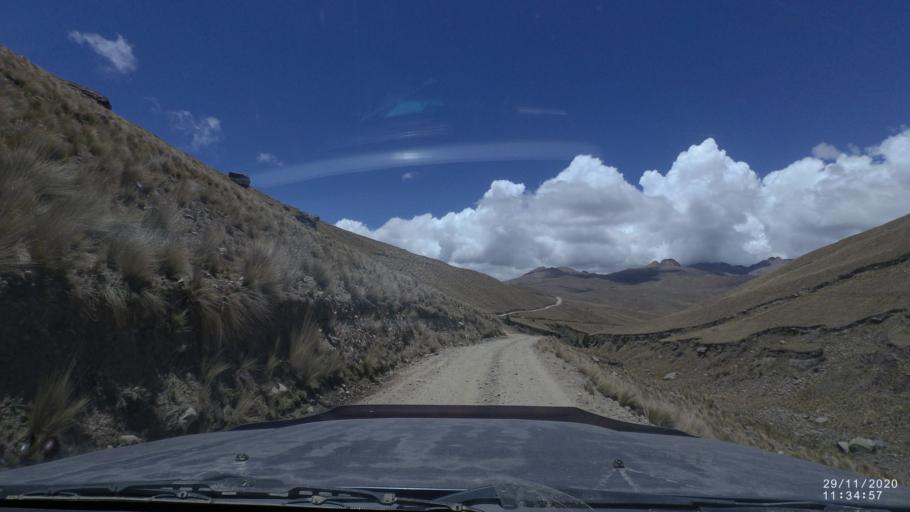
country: BO
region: Cochabamba
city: Cochabamba
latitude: -17.1906
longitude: -66.2225
